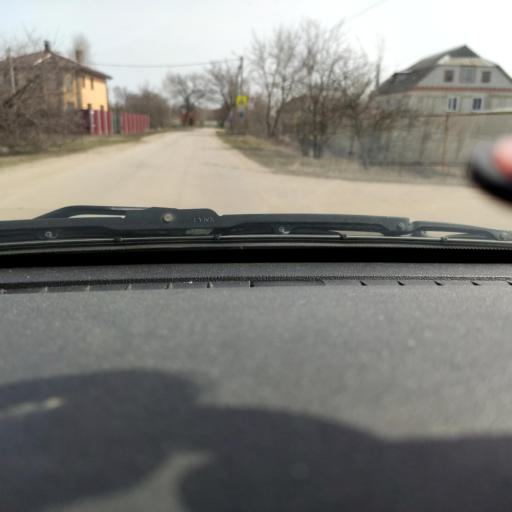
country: RU
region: Voronezj
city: Novaya Usman'
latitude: 51.6271
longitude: 39.4138
